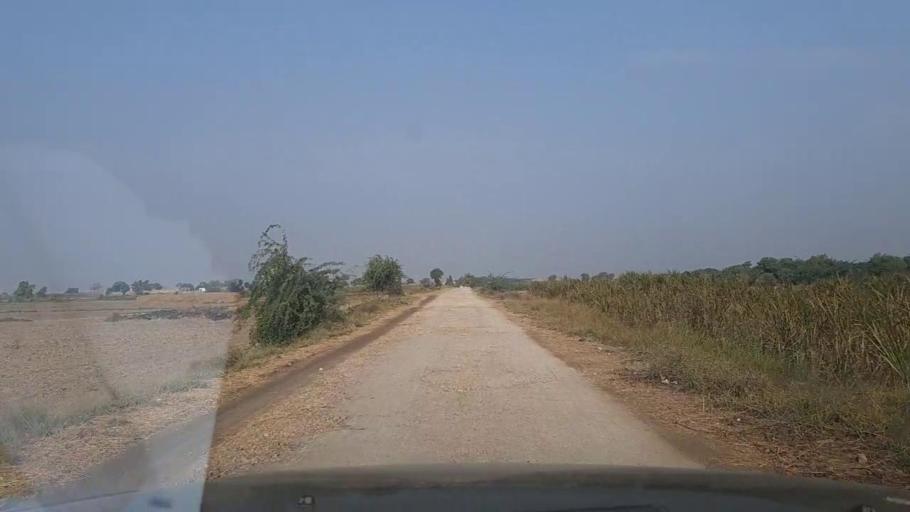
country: PK
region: Sindh
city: Bulri
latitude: 24.9369
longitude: 68.2830
